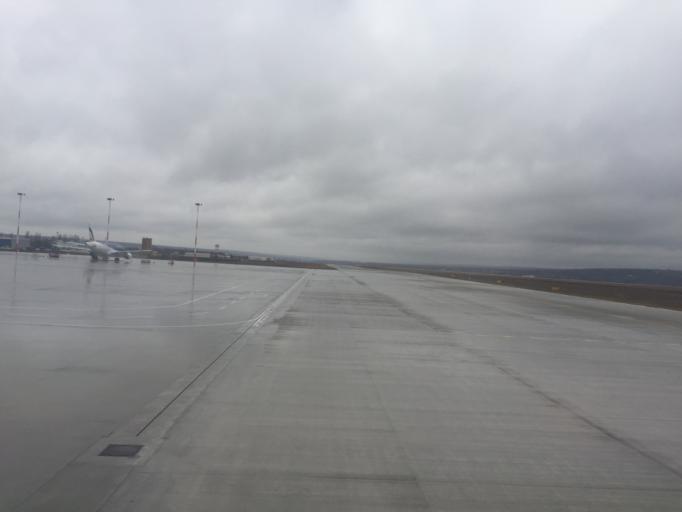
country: MD
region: Chisinau
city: Singera
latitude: 46.9318
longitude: 28.9345
